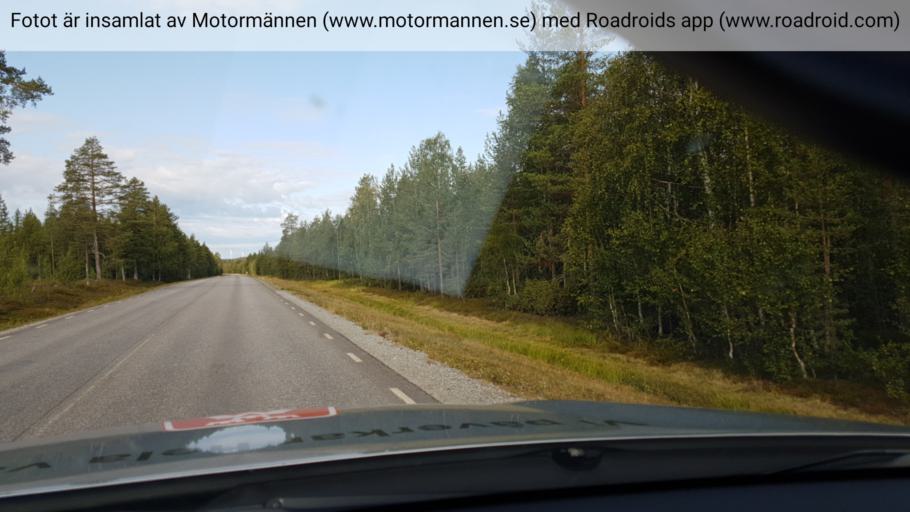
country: SE
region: Norrbotten
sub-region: Pitea Kommun
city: Roknas
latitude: 65.3417
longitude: 20.9688
